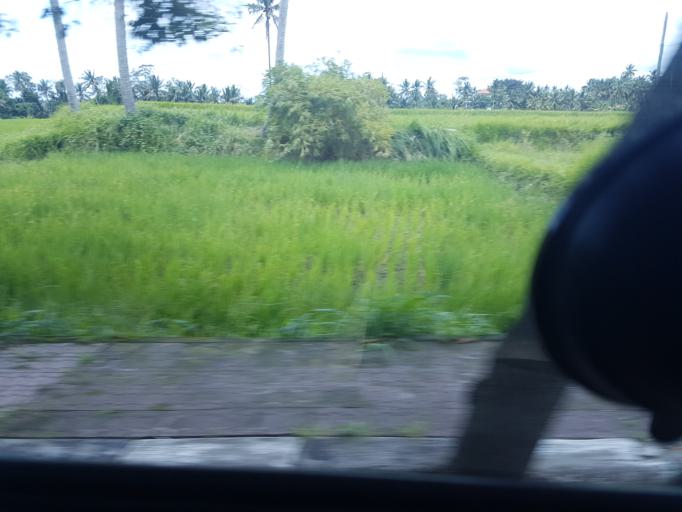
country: ID
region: Bali
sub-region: Kabupaten Gianyar
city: Ubud
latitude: -8.5196
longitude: 115.2932
